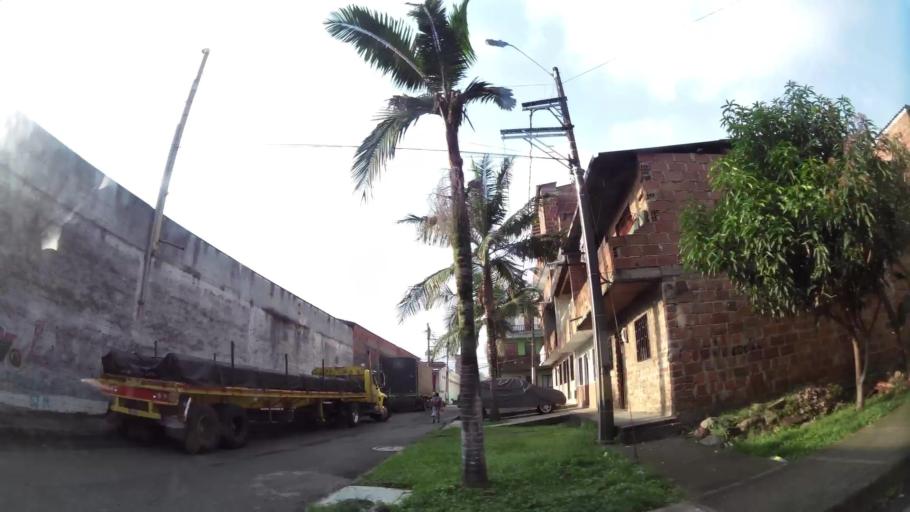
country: CO
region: Antioquia
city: Sabaneta
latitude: 6.1662
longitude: -75.6181
